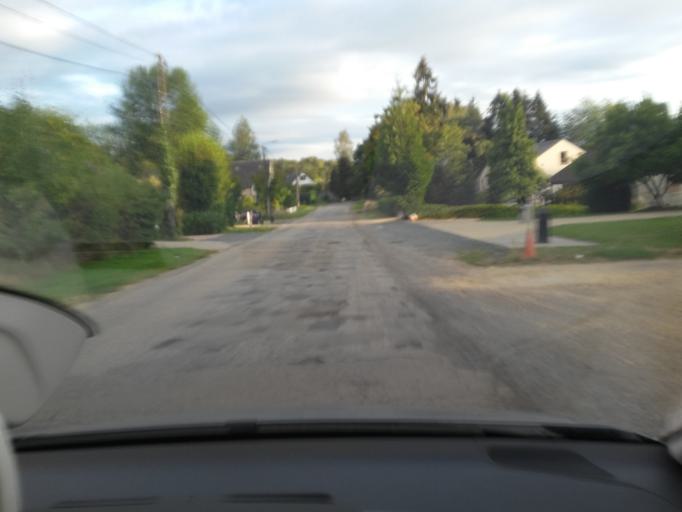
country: BE
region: Wallonia
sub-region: Province du Luxembourg
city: Arlon
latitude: 49.7018
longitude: 5.8126
